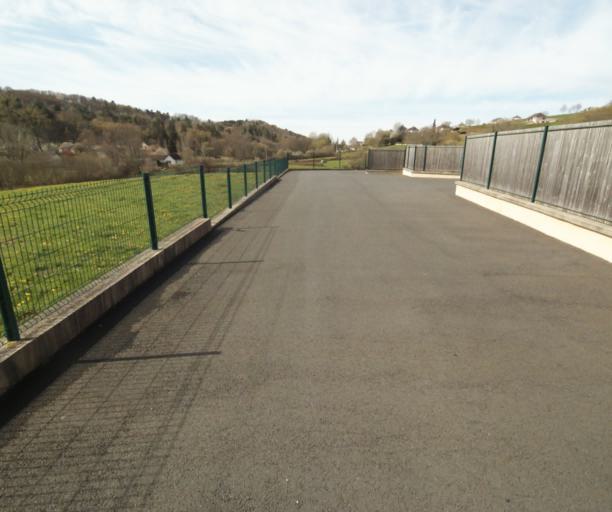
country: FR
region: Limousin
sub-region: Departement de la Correze
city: Laguenne
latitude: 45.2648
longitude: 1.8170
